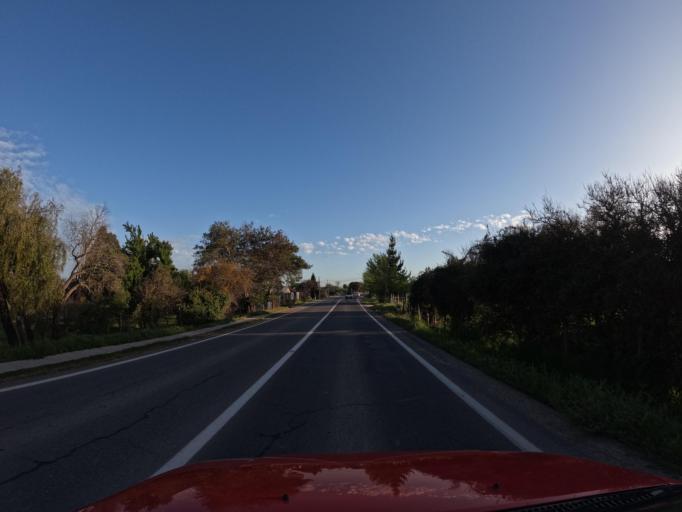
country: CL
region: O'Higgins
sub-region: Provincia de Colchagua
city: Santa Cruz
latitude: -34.2557
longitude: -71.7280
